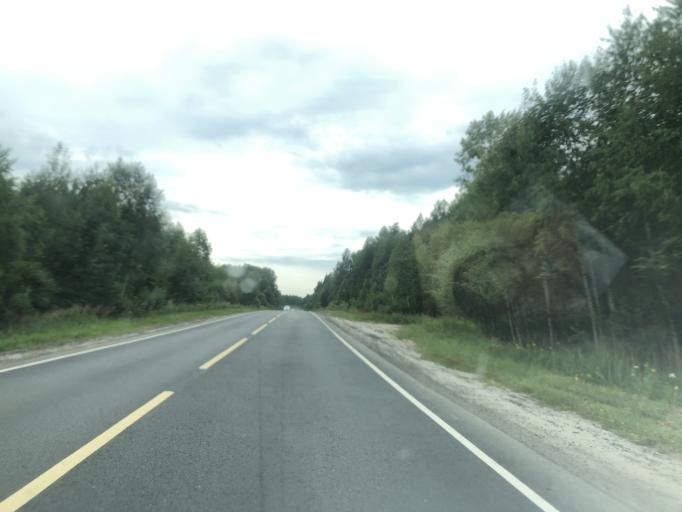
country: RU
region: Ivanovo
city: Pestyaki
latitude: 56.7077
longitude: 42.7781
